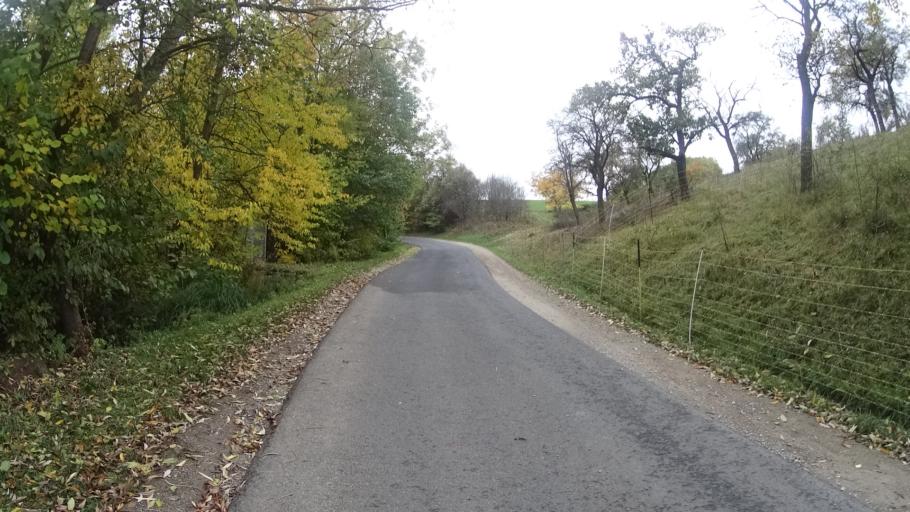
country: DE
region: Thuringia
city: Apfelstadt
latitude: 50.8499
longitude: 10.8798
